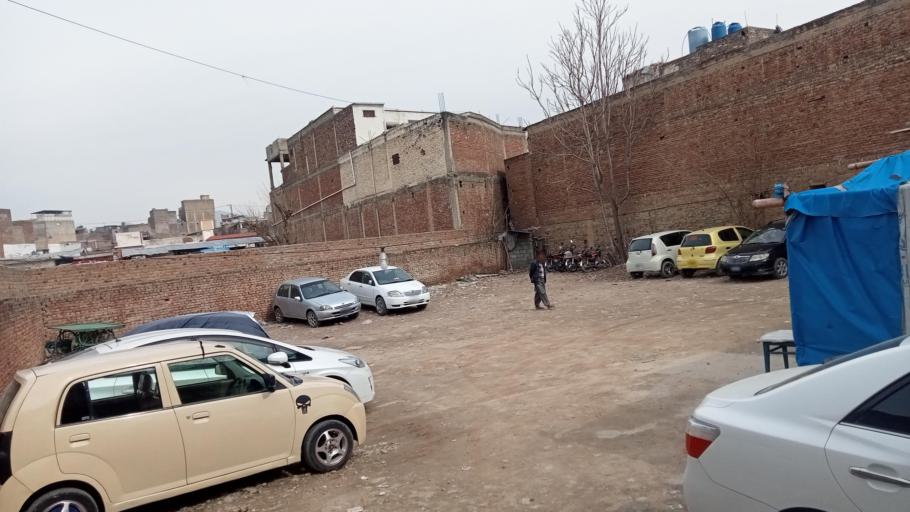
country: PK
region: Khyber Pakhtunkhwa
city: Mingora
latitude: 34.7700
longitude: 72.3611
